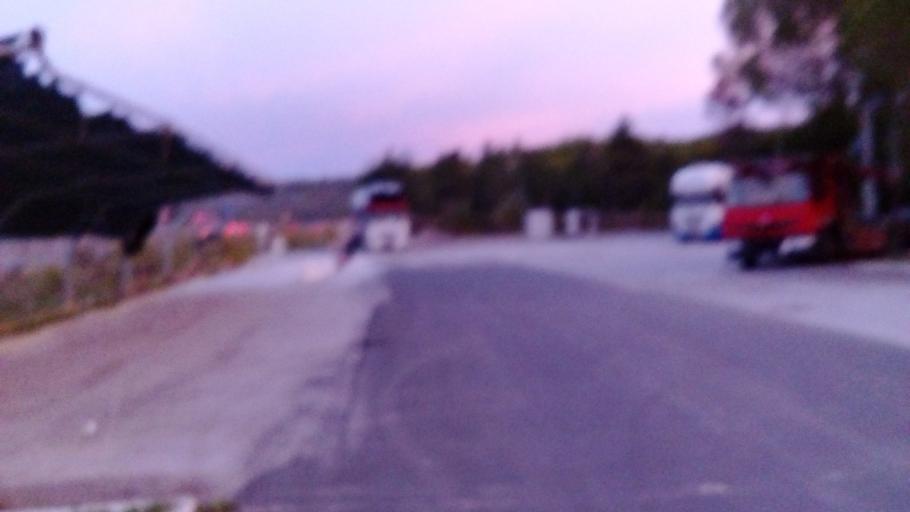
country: IT
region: Tuscany
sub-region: Provincia di Grosseto
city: Civitella Marittima
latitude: 43.0290
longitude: 11.2781
